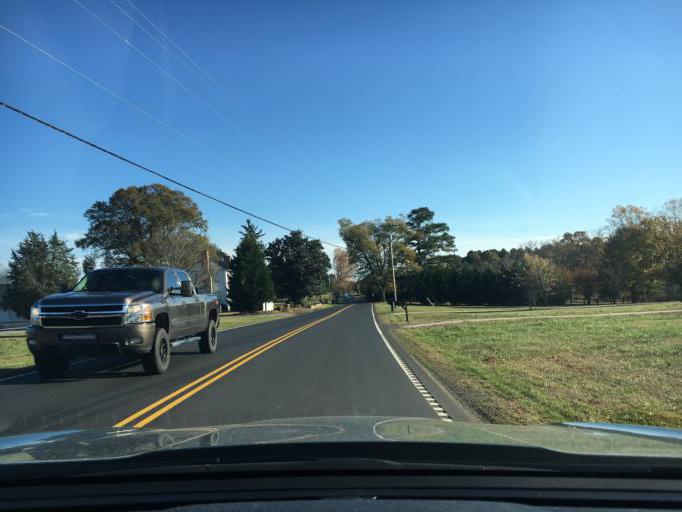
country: US
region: South Carolina
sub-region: Spartanburg County
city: Inman
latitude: 35.0236
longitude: -82.0851
